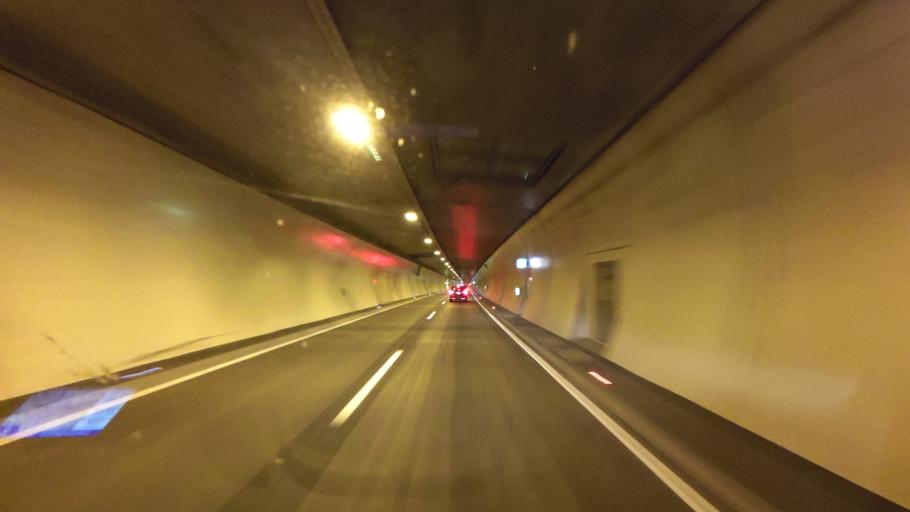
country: AT
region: Salzburg
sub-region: Politischer Bezirk Tamsweg
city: Sankt Michael im Lungau
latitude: 47.0319
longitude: 13.5990
